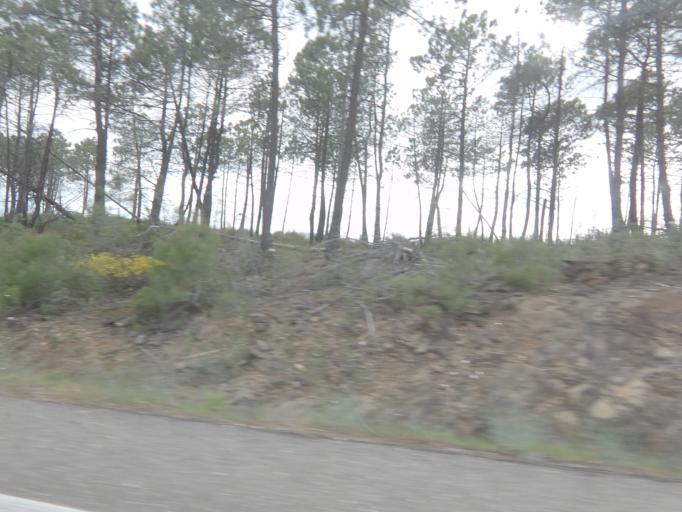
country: ES
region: Extremadura
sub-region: Provincia de Caceres
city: Acebo
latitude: 40.2066
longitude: -6.6747
